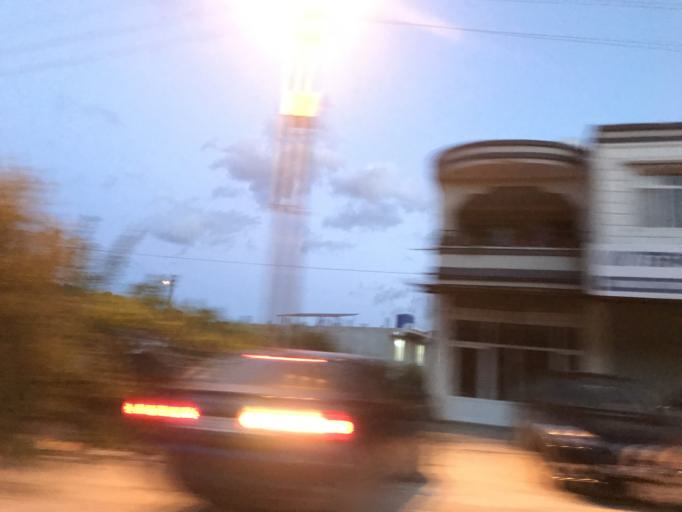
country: TR
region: Hatay
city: Karacay
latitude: 36.1476
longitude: 36.0819
